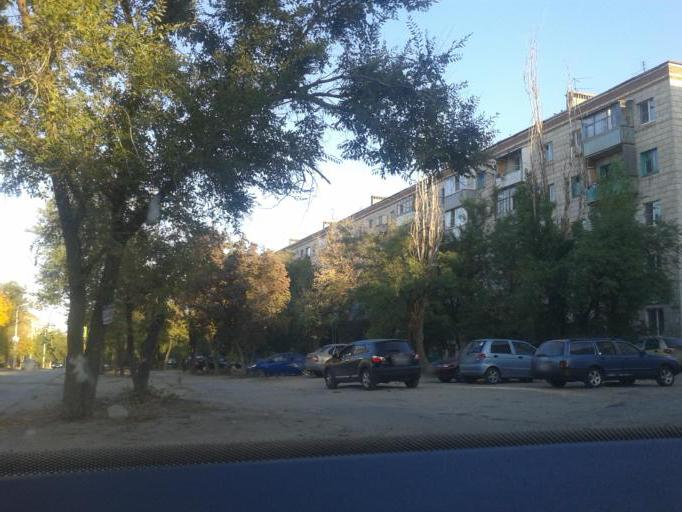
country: RU
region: Volgograd
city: Gorodishche
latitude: 48.7702
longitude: 44.4798
